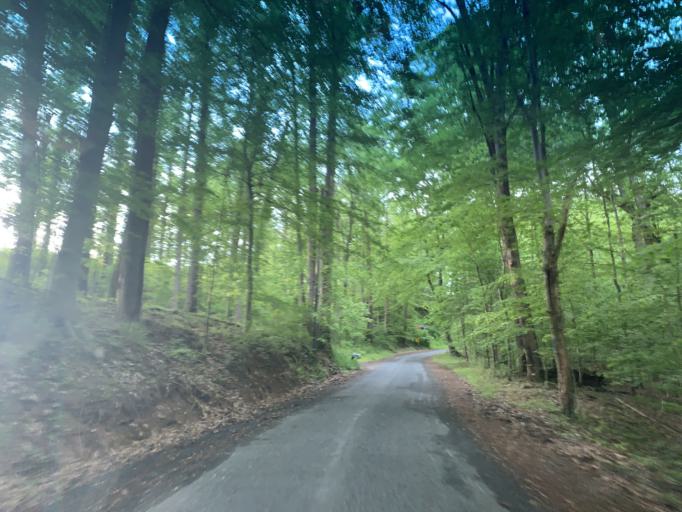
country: US
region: Pennsylvania
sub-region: York County
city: Susquehanna Trails
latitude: 39.7028
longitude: -76.2613
